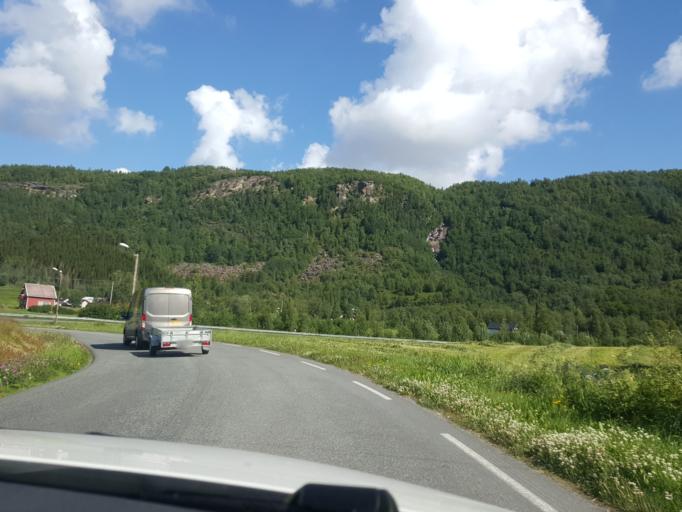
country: NO
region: Nordland
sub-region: Bodo
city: Loding
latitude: 67.1191
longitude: 15.0133
